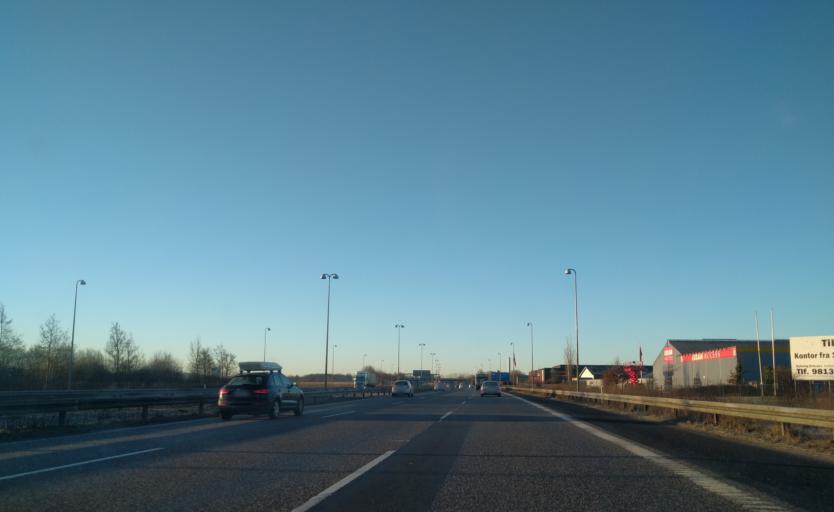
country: DK
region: North Denmark
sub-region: Alborg Kommune
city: Aalborg
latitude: 57.0779
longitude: 9.9590
